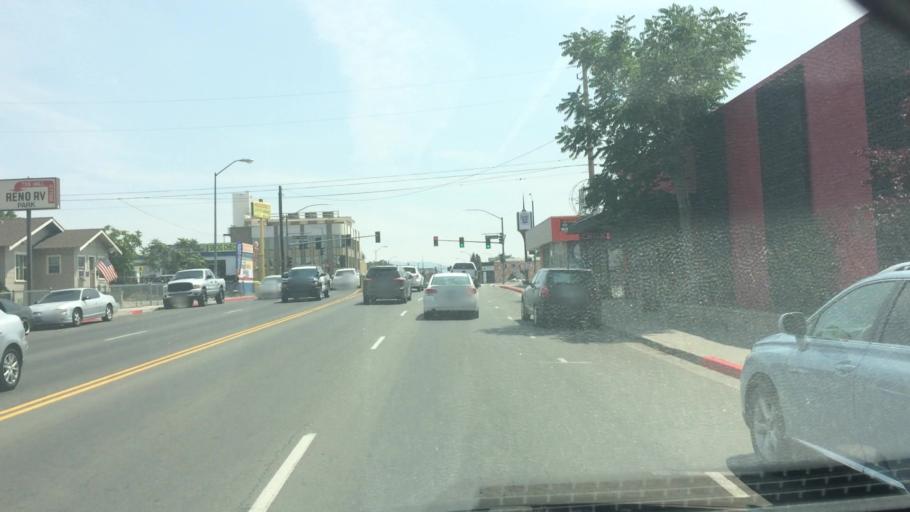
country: US
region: Nevada
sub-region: Washoe County
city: Reno
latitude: 39.5267
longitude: -119.8031
